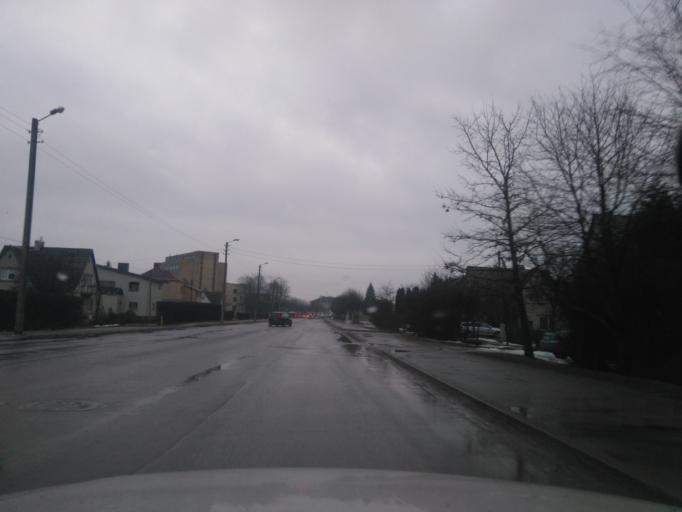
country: LT
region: Kauno apskritis
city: Dainava (Kaunas)
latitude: 54.8947
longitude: 23.9560
